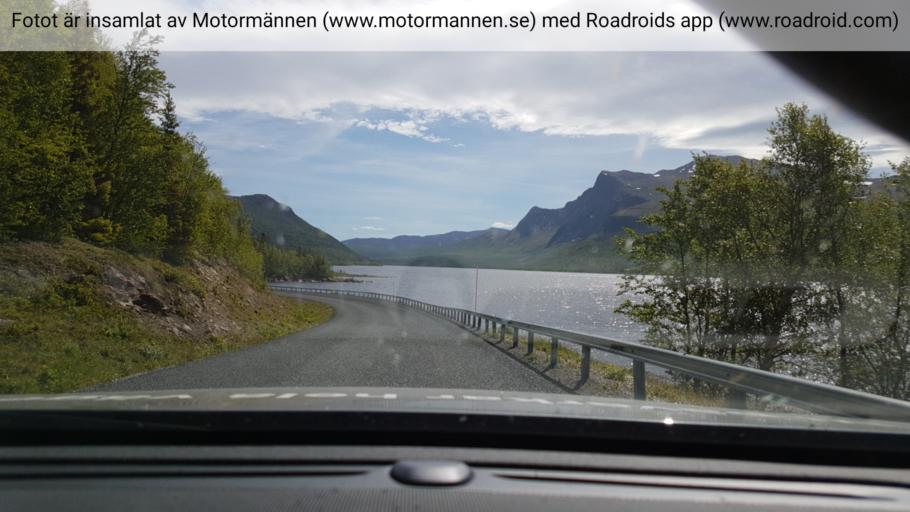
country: SE
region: Vaesterbotten
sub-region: Vilhelmina Kommun
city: Sjoberg
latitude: 65.2602
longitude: 15.3862
